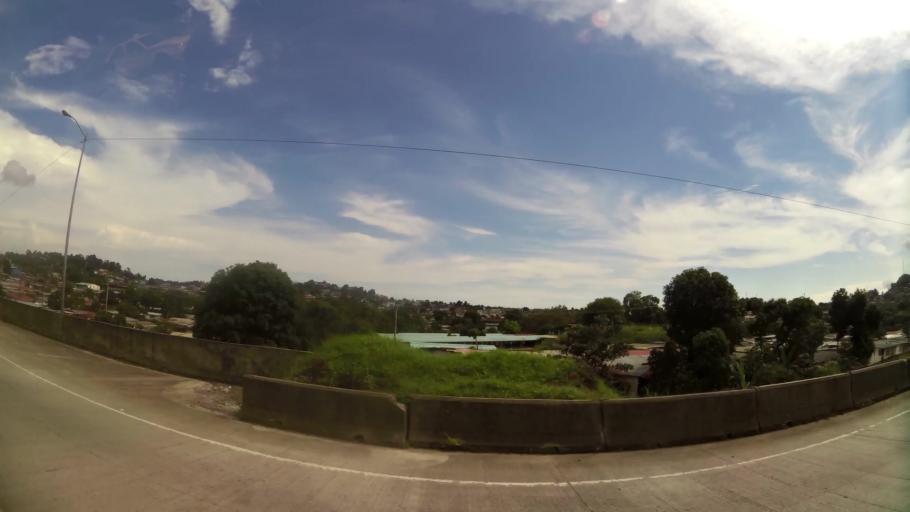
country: PA
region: Panama
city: San Miguelito
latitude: 9.0714
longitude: -79.4935
